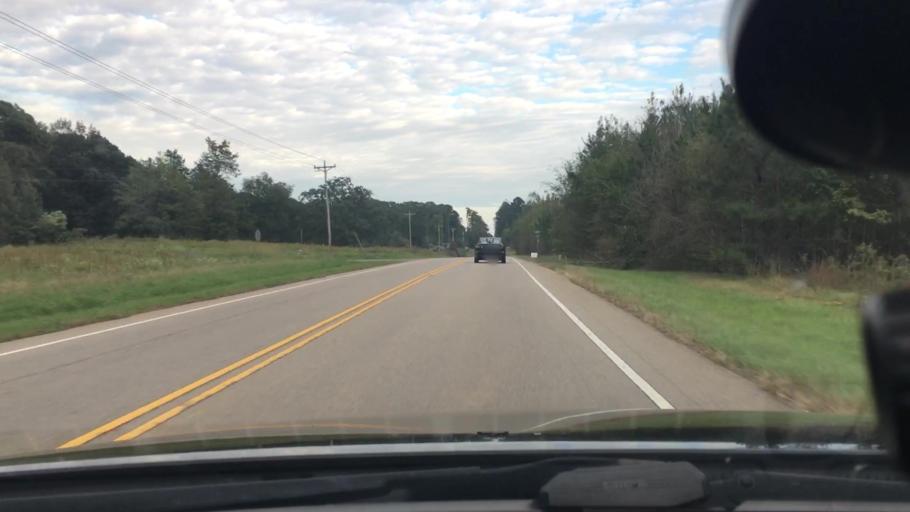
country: US
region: North Carolina
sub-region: Moore County
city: Robbins
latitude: 35.3966
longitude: -79.5335
